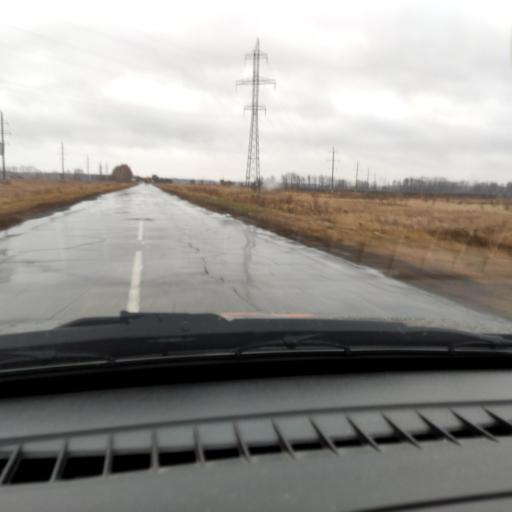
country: RU
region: Samara
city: Khryashchevka
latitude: 53.7332
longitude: 49.1869
